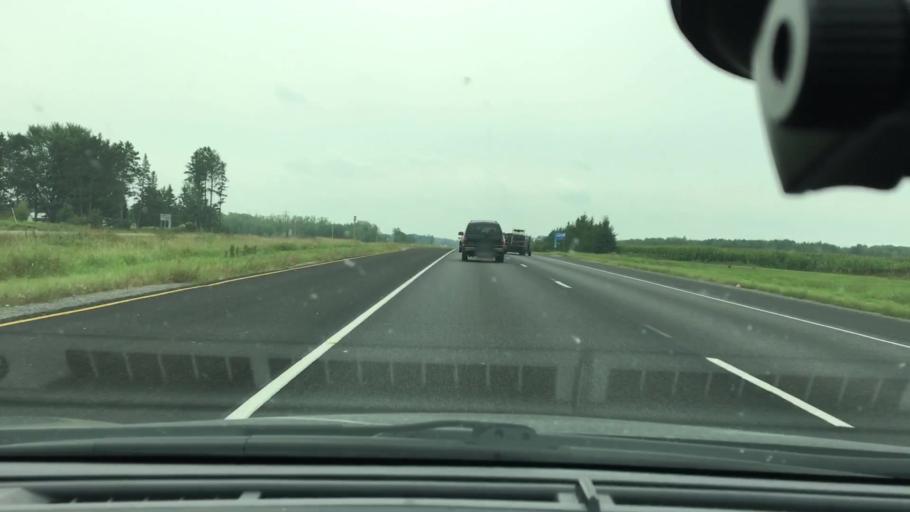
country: US
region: Minnesota
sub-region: Mille Lacs County
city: Milaca
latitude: 45.8491
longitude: -93.6622
